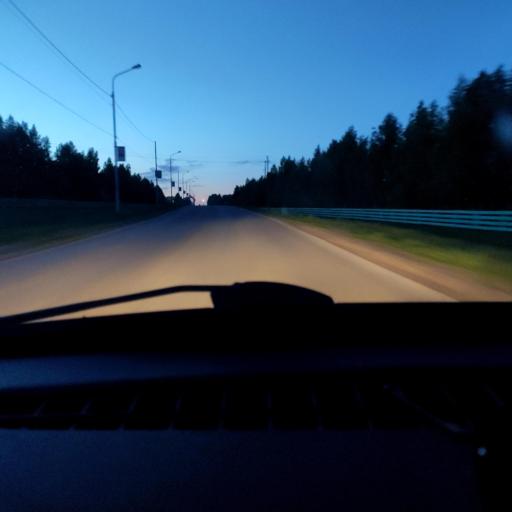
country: RU
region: Bashkortostan
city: Karmaskaly
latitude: 54.3757
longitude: 56.1757
